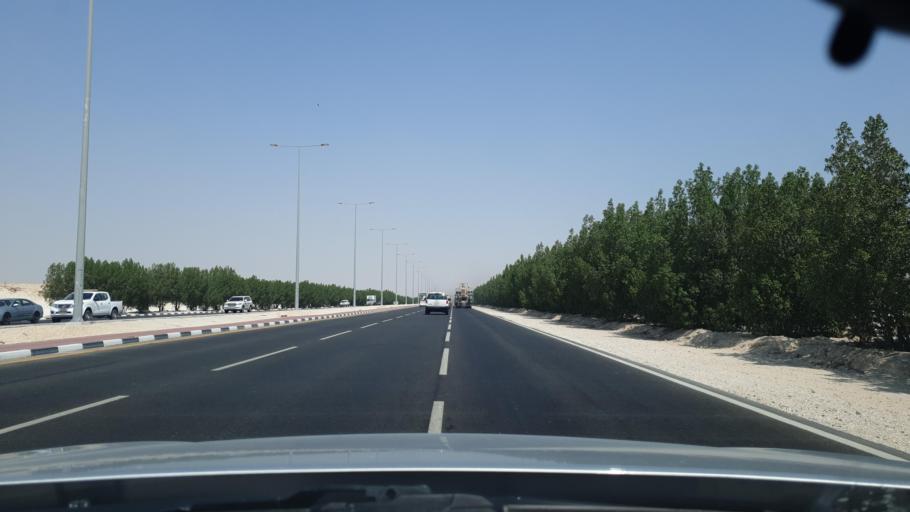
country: QA
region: Al Khawr
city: Al Khawr
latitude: 25.6988
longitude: 51.5028
